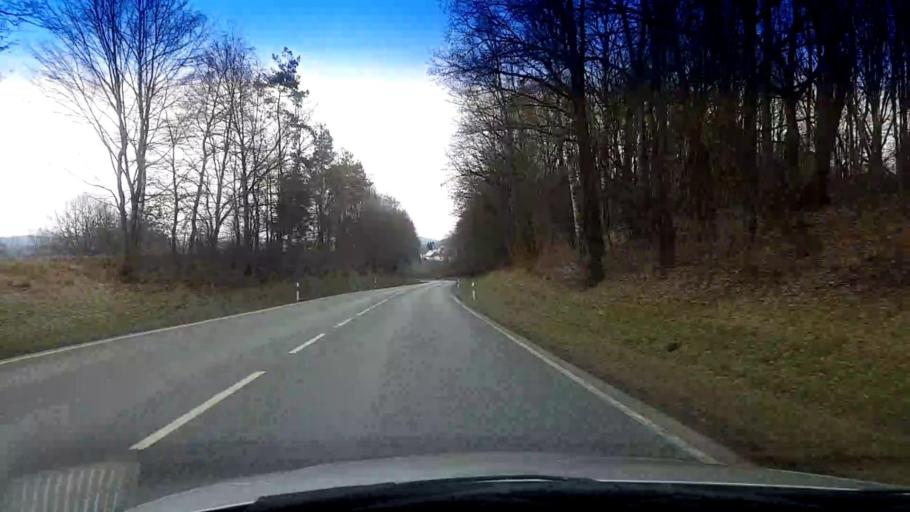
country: DE
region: Bavaria
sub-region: Upper Franconia
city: Kulmbach
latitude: 50.0899
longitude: 11.4536
